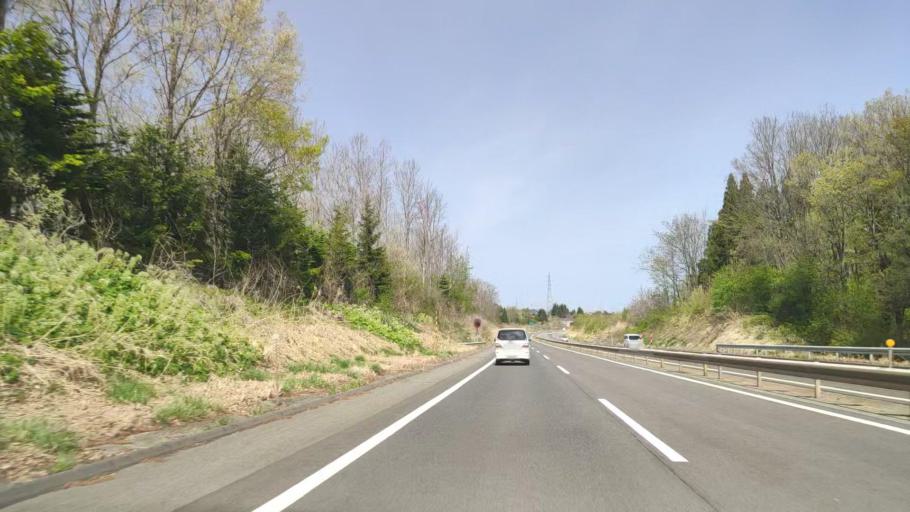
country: JP
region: Aomori
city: Hachinohe
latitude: 40.4732
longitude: 141.4609
